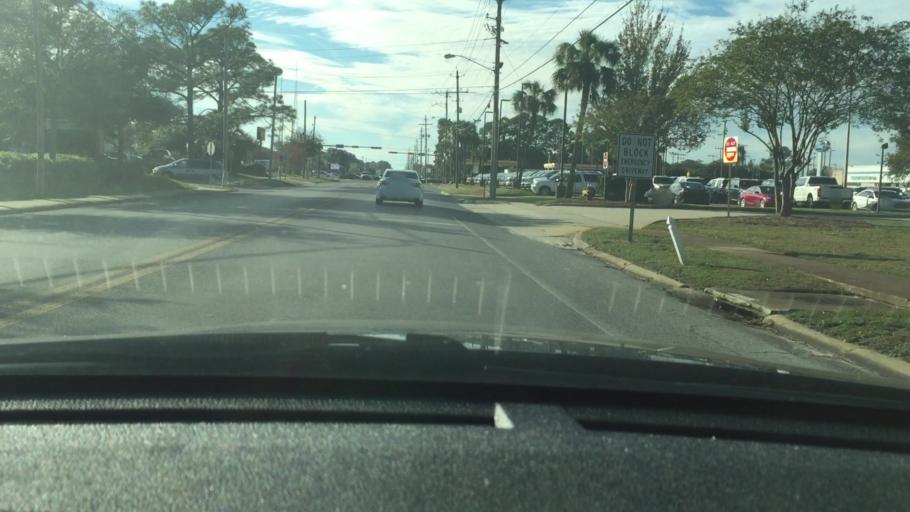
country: US
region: Florida
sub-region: Okaloosa County
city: Fort Walton Beach
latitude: 30.4125
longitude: -86.6114
